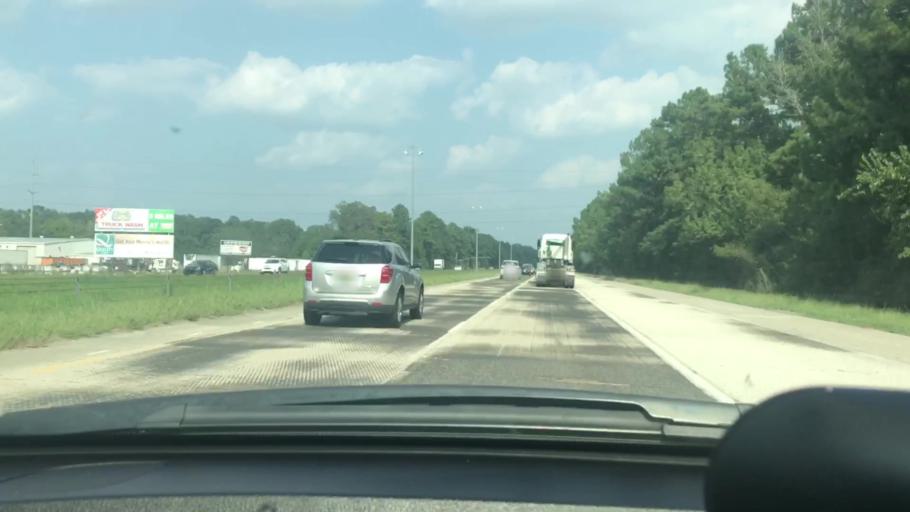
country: US
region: Louisiana
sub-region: Tangipahoa Parish
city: Hammond
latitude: 30.4794
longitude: -90.5170
